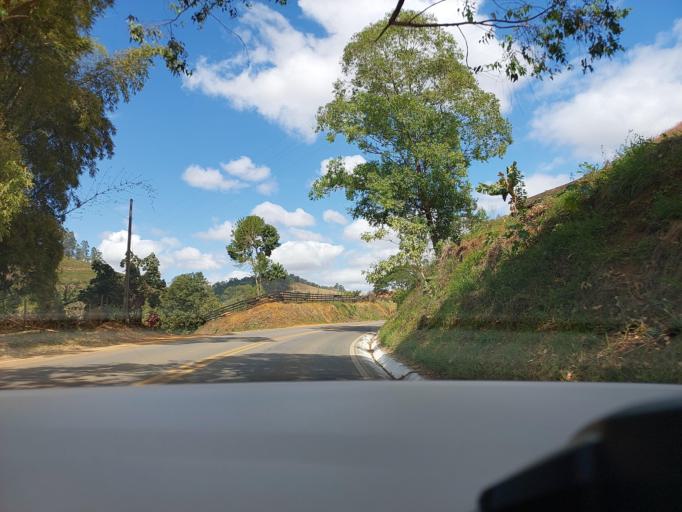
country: BR
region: Minas Gerais
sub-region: Mirai
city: Mirai
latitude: -20.9989
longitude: -42.5491
